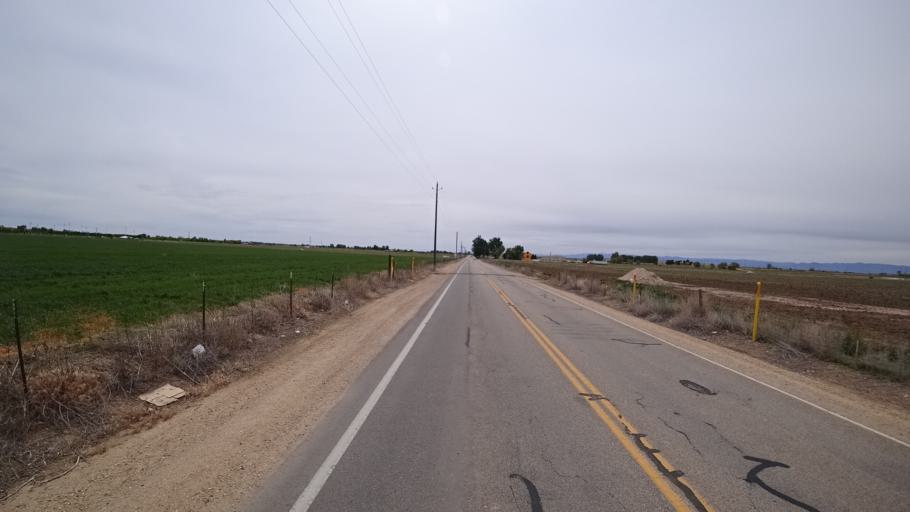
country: US
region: Idaho
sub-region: Ada County
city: Meridian
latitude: 43.5485
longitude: -116.3746
